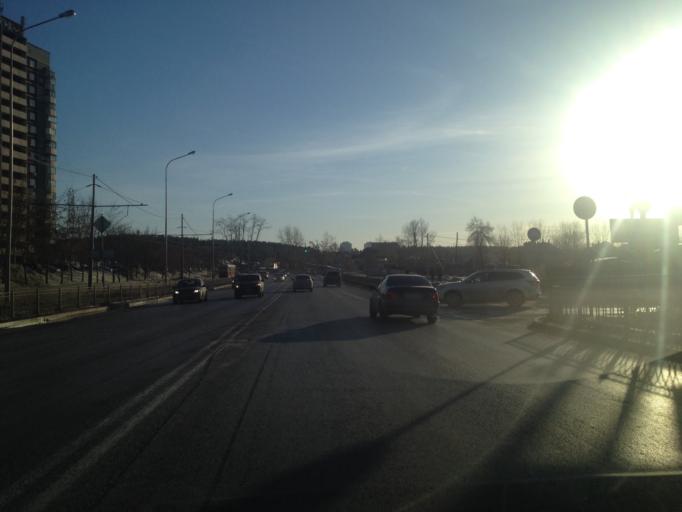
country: RU
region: Sverdlovsk
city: Shirokaya Rechka
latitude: 56.8217
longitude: 60.5385
